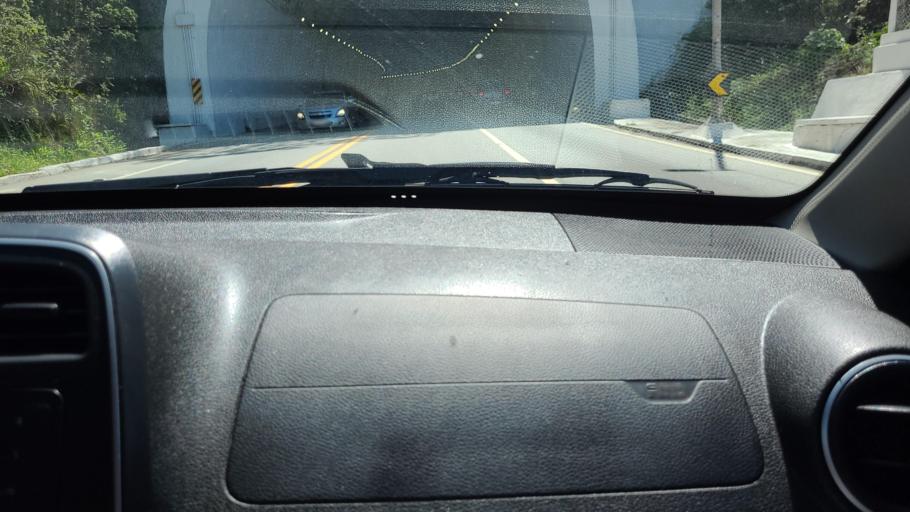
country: BR
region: Sao Paulo
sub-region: Campos Do Jordao
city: Campos do Jordao
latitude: -22.8458
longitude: -45.6151
